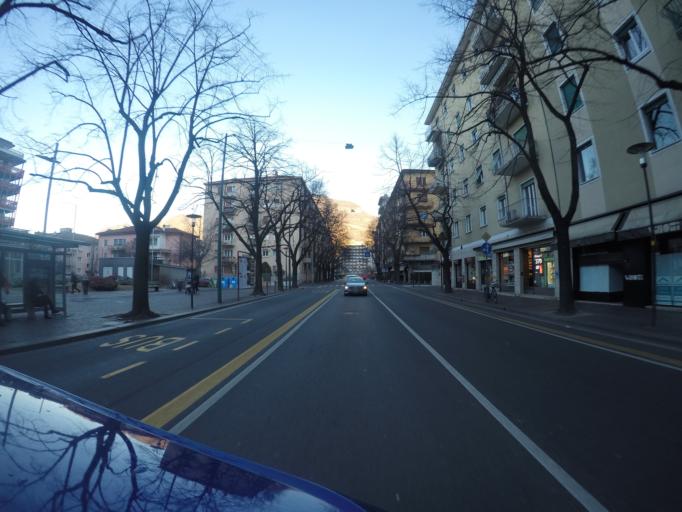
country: IT
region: Trentino-Alto Adige
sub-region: Bolzano
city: Bolzano
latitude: 46.4934
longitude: 11.3409
